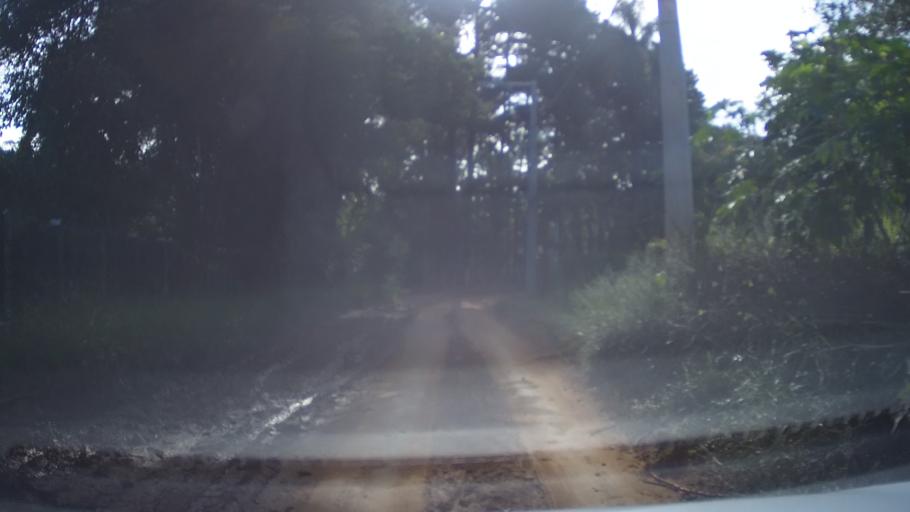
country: BR
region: Sao Paulo
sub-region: Itupeva
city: Itupeva
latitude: -23.2166
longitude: -47.0679
